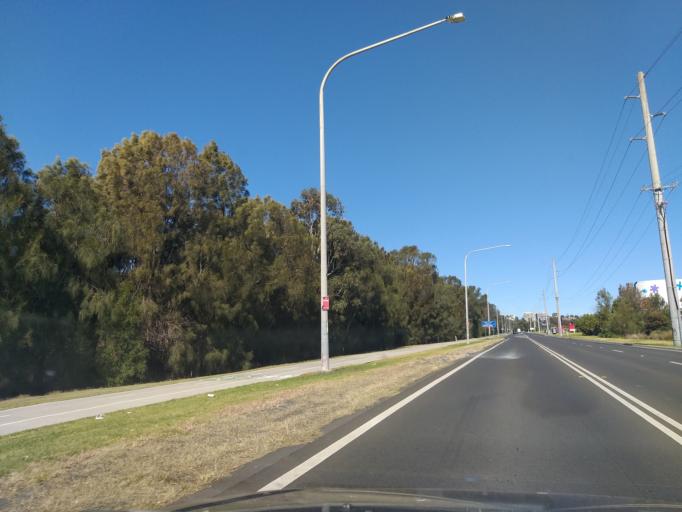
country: AU
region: New South Wales
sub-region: Wollongong
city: Fairy Meadow
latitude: -34.3998
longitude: 150.9008
